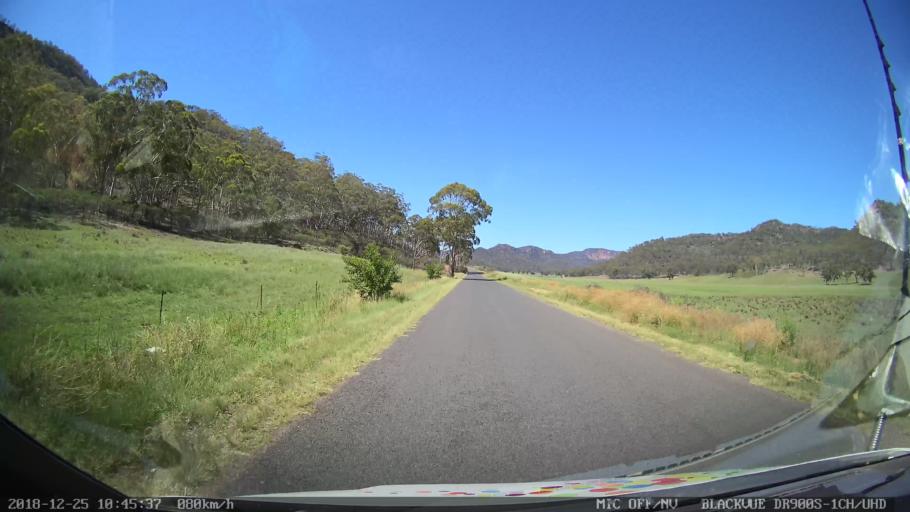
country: AU
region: New South Wales
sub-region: Upper Hunter Shire
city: Merriwa
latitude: -32.4351
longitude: 150.2890
